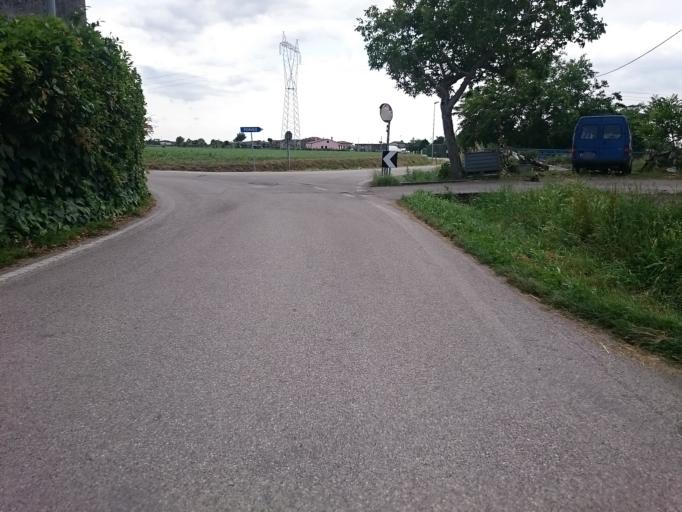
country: IT
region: Veneto
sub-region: Provincia di Padova
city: Ponso
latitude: 45.1919
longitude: 11.5954
